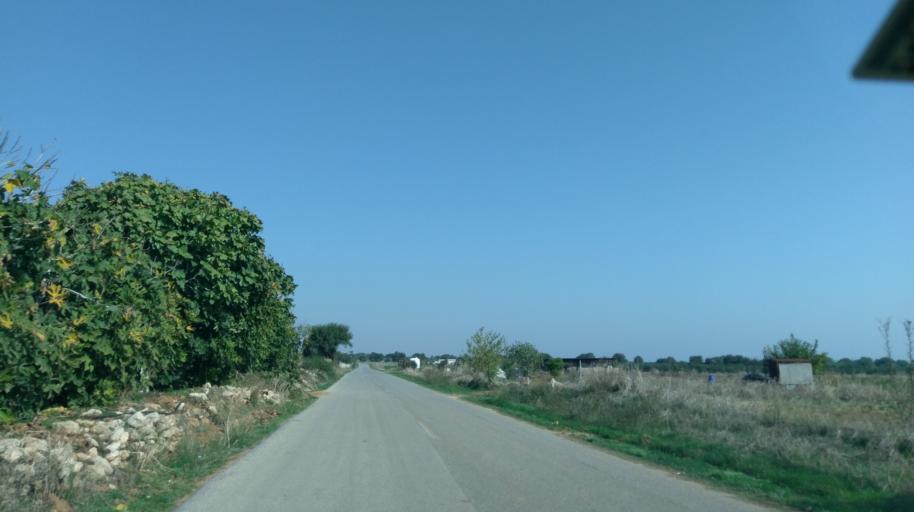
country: CY
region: Ammochostos
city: Leonarisso
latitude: 35.4855
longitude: 34.1997
